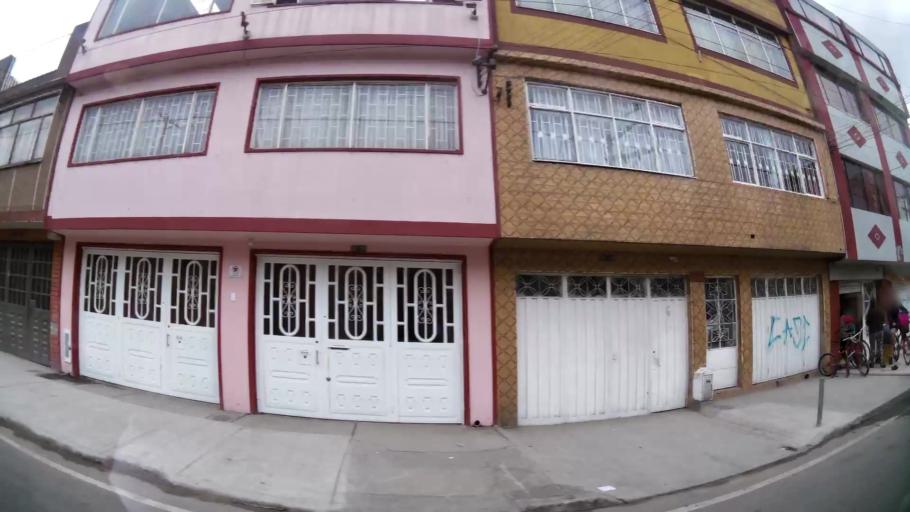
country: CO
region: Bogota D.C.
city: Bogota
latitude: 4.6737
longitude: -74.0939
